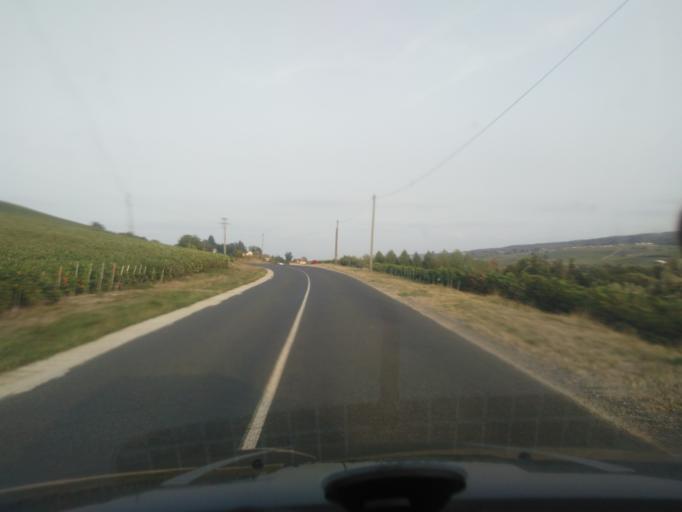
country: FR
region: Champagne-Ardenne
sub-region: Departement de la Marne
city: Mareuil-le-Port
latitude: 49.0808
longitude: 3.8064
